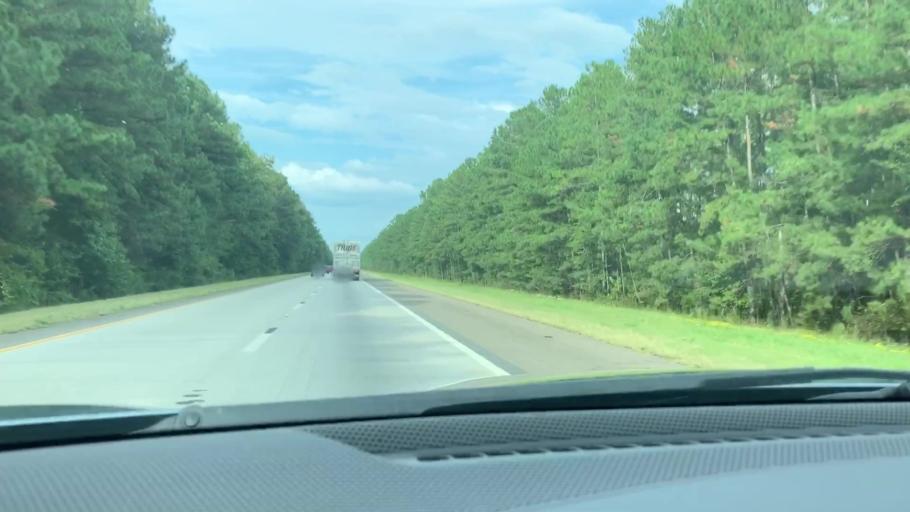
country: US
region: South Carolina
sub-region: Colleton County
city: Walterboro
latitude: 33.0523
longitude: -80.6667
